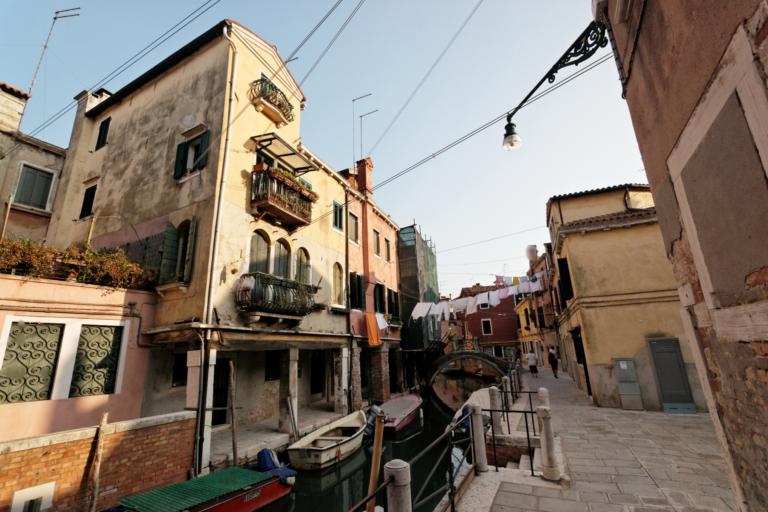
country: IT
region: Veneto
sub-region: Provincia di Venezia
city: Venice
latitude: 45.4334
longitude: 12.3567
